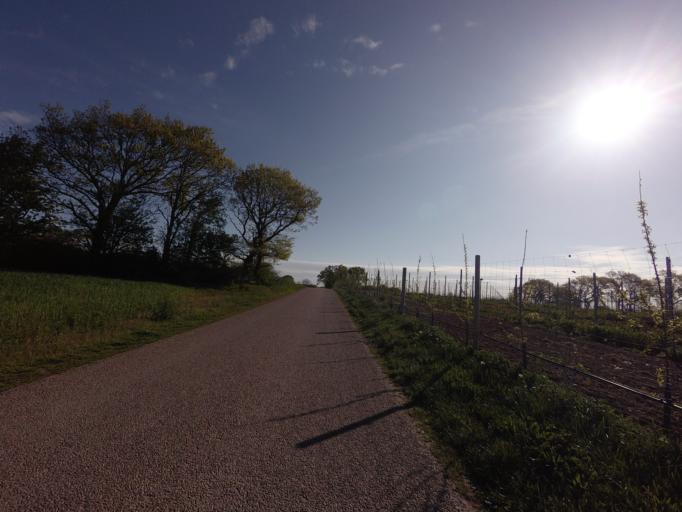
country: SE
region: Skane
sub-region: Hoganas Kommun
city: Hoganas
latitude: 56.2597
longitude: 12.5463
